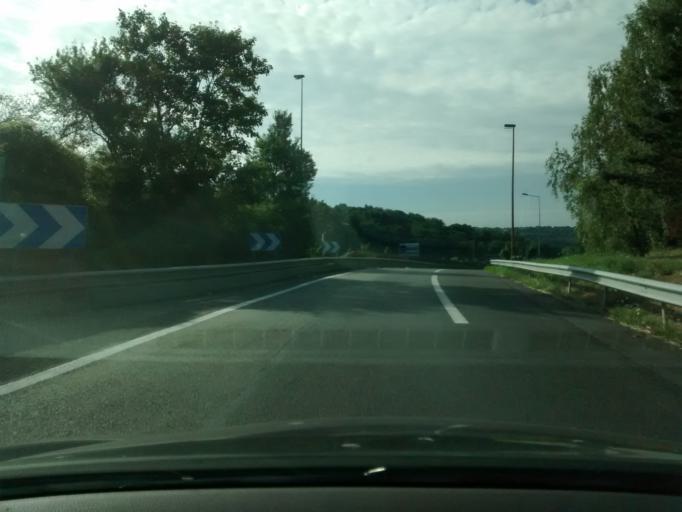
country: FR
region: Ile-de-France
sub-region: Departement de l'Essonne
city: Bievres
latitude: 48.7757
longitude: 2.2281
